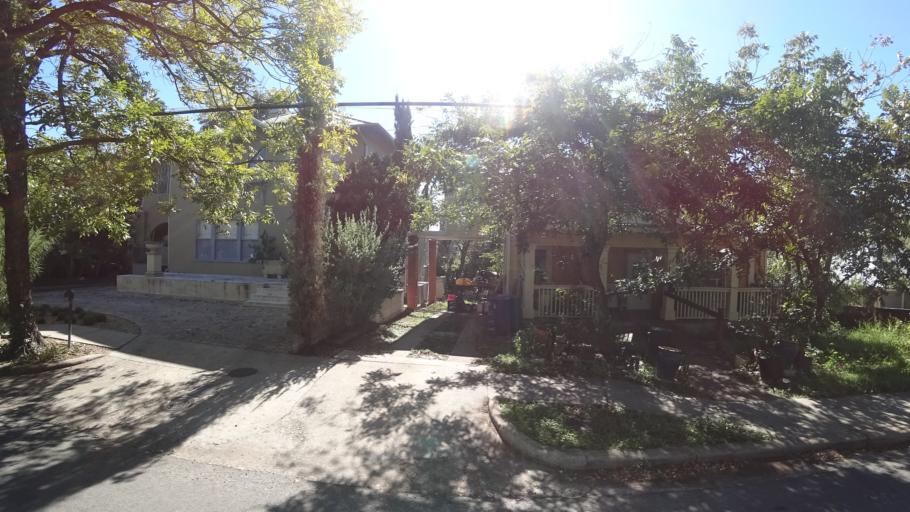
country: US
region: Texas
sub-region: Travis County
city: Austin
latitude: 30.2756
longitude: -97.7566
